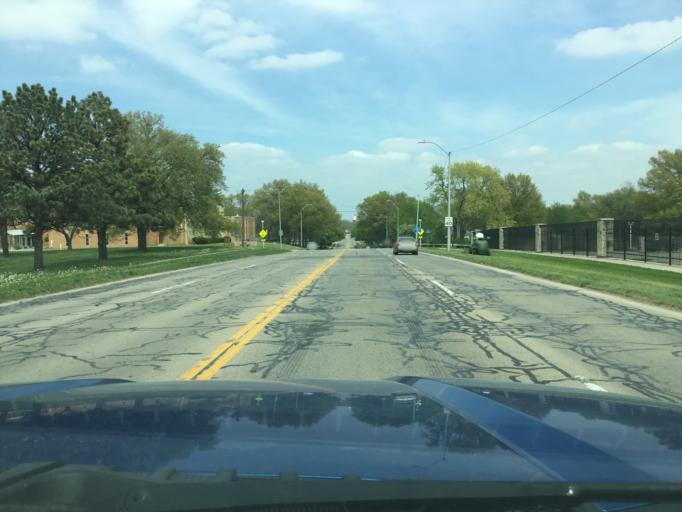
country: US
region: Kansas
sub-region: Shawnee County
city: Topeka
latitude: 39.0215
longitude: -95.6857
